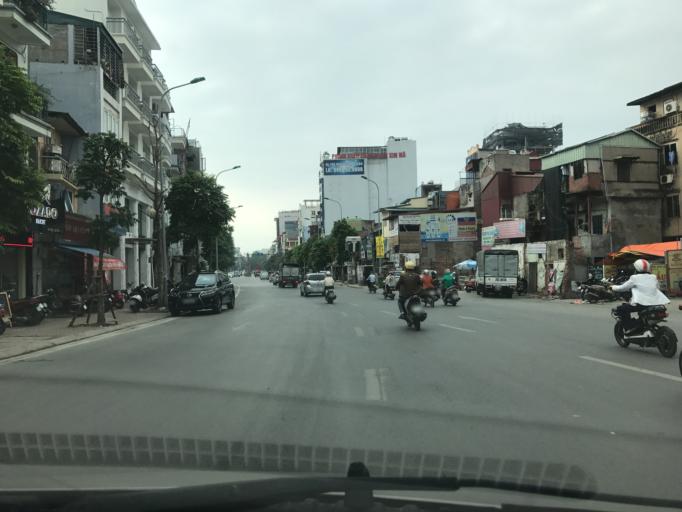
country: VN
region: Ha Noi
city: Dong Da
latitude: 21.0327
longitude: 105.8302
